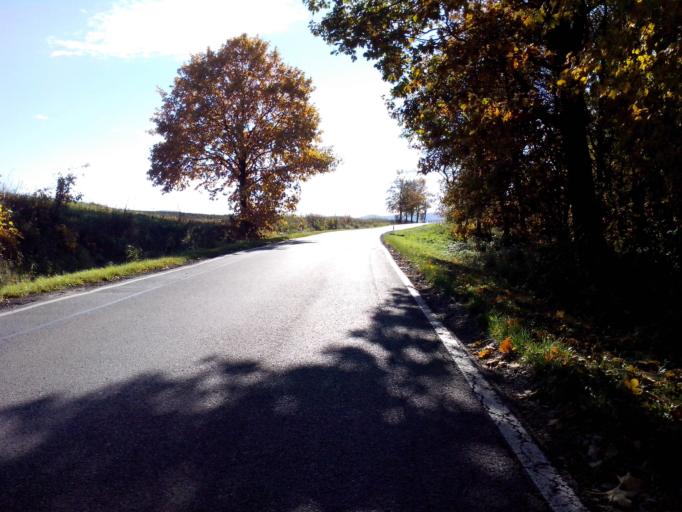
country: PL
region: Subcarpathian Voivodeship
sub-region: Powiat strzyzowski
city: Jawornik
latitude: 49.7989
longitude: 21.8631
